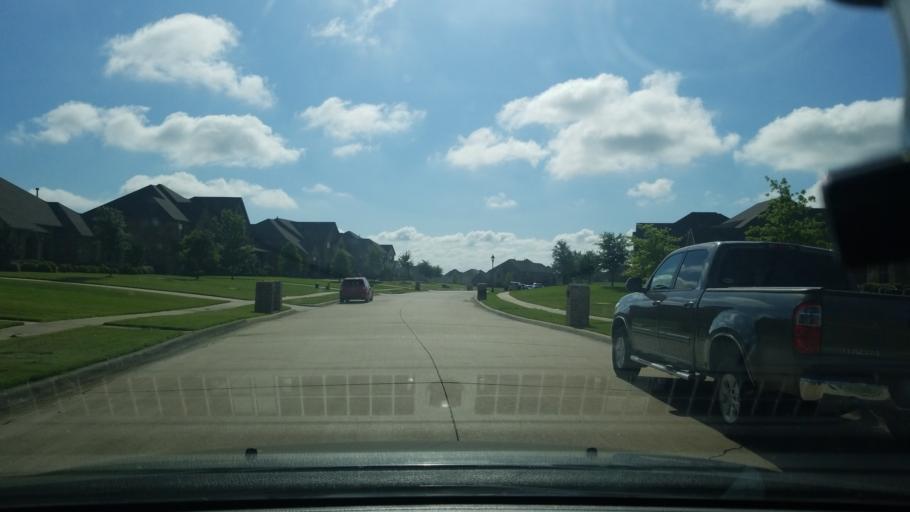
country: US
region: Texas
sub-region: Dallas County
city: Sunnyvale
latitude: 32.8052
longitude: -96.5685
